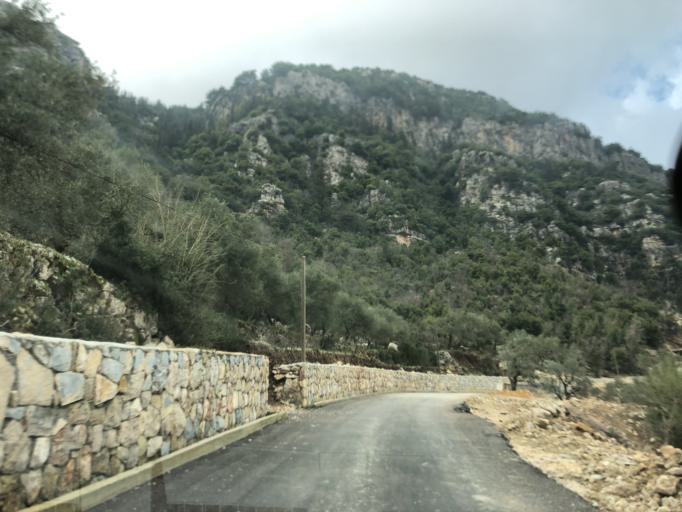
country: LB
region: Liban-Nord
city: Amioun
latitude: 34.2056
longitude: 35.8332
